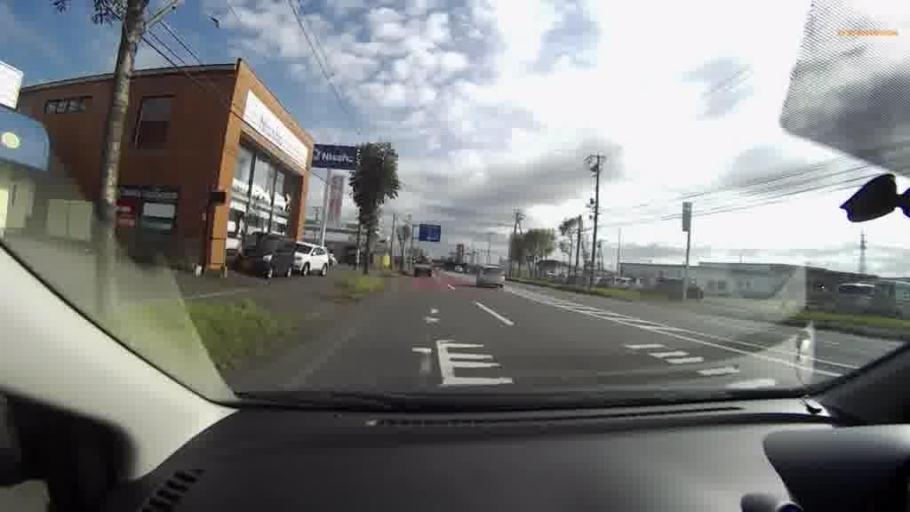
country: JP
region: Hokkaido
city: Kushiro
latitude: 43.0127
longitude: 144.3058
